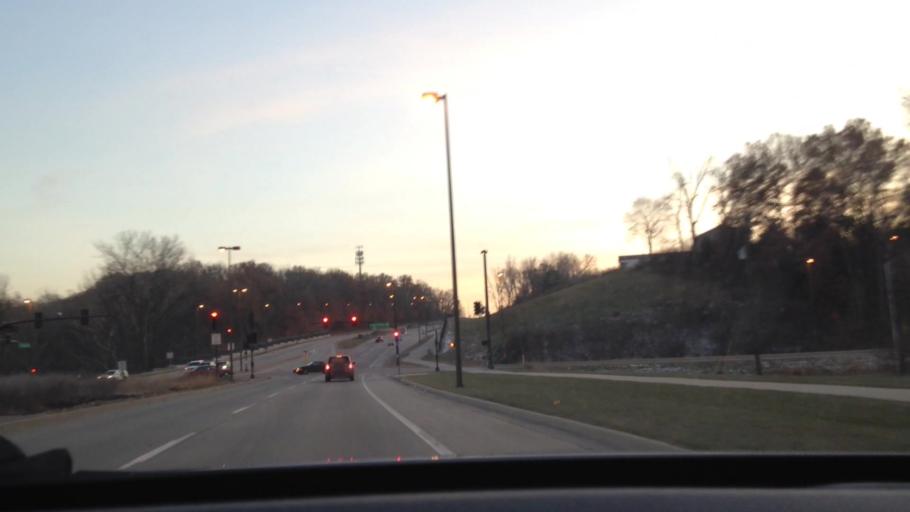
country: US
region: Missouri
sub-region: Clay County
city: North Kansas City
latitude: 39.1633
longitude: -94.5325
